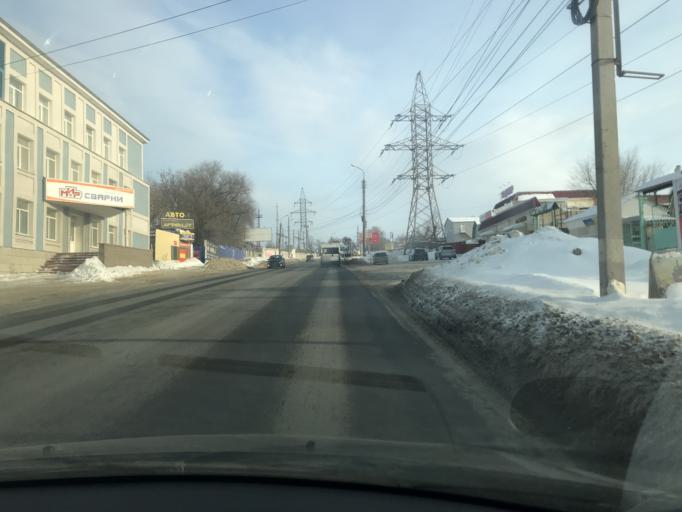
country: RU
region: Ulyanovsk
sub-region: Ulyanovskiy Rayon
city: Ulyanovsk
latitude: 54.3305
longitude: 48.3628
